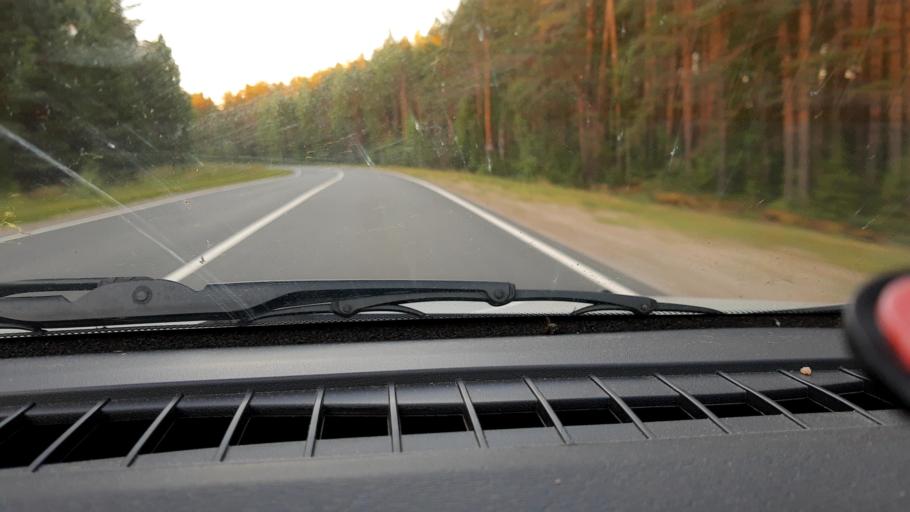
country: RU
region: Nizjnij Novgorod
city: Krasnyye Baki
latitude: 57.2158
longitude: 45.4800
